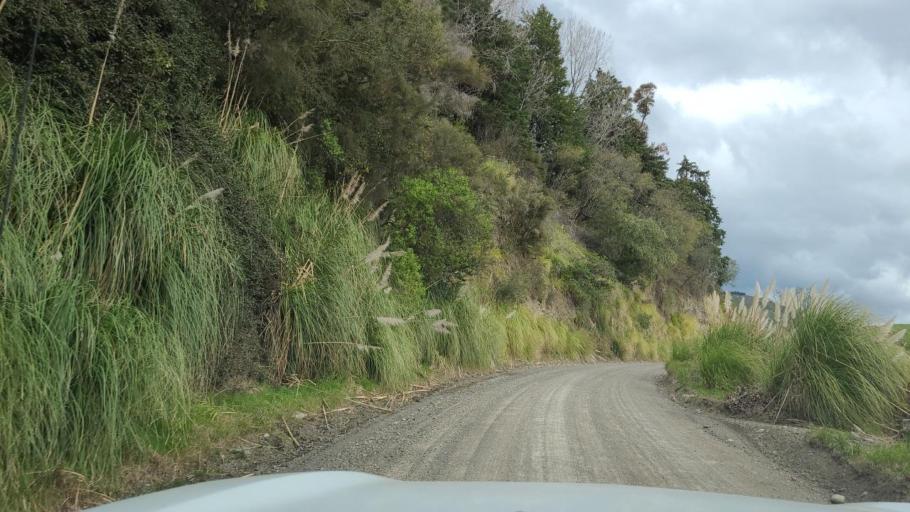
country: NZ
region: Hawke's Bay
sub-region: Napier City
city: Napier
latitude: -39.1794
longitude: 176.9720
